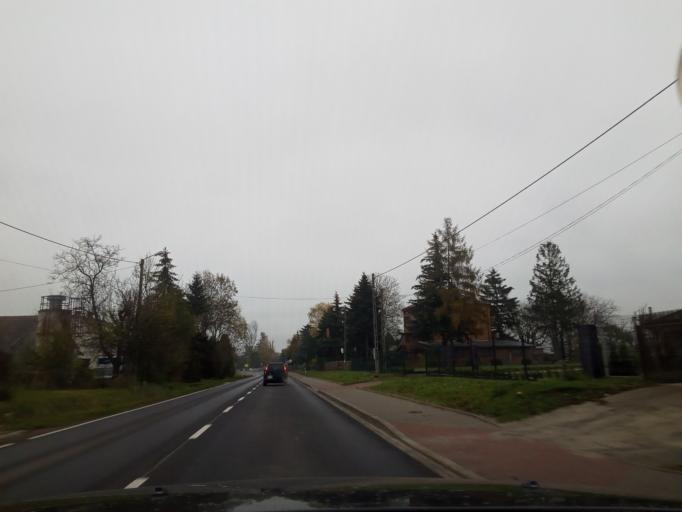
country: PL
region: Lesser Poland Voivodeship
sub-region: Powiat proszowicki
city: Proszowice
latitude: 50.1783
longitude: 20.2526
